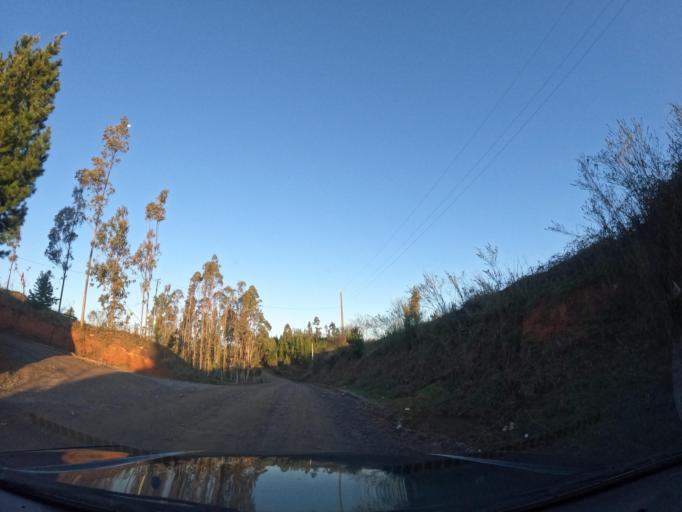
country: CL
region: Biobio
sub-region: Provincia de Concepcion
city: Chiguayante
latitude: -37.0139
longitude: -72.8622
